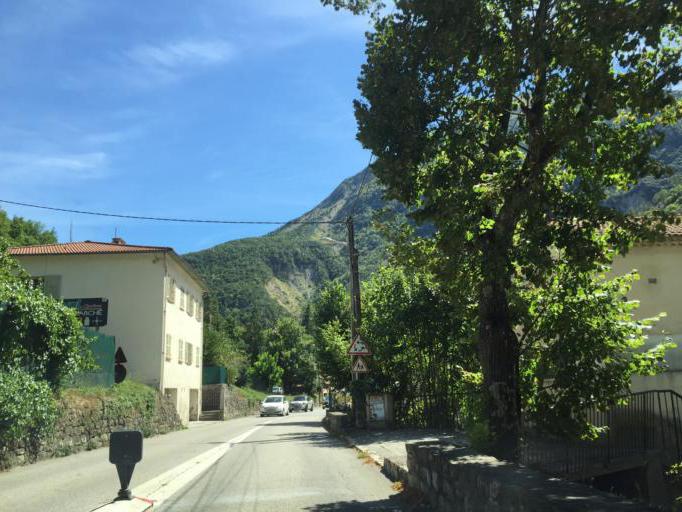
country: FR
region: Provence-Alpes-Cote d'Azur
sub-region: Departement des Alpes-Maritimes
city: Gilette
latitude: 43.9776
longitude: 7.1406
